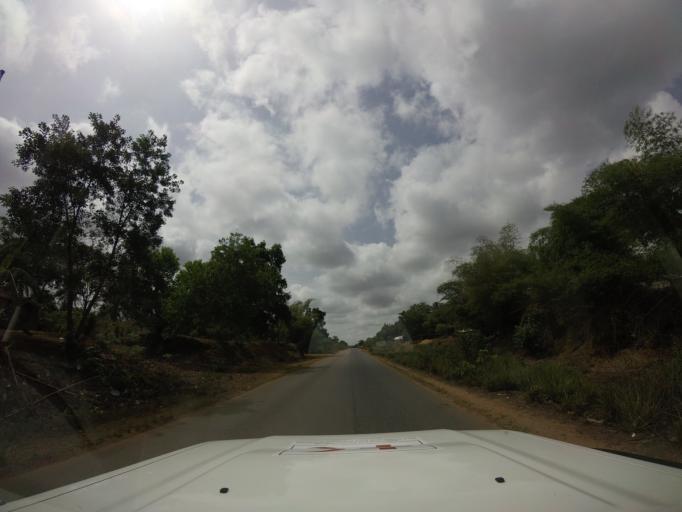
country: LR
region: Montserrado
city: Monrovia
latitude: 6.4792
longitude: -10.8122
